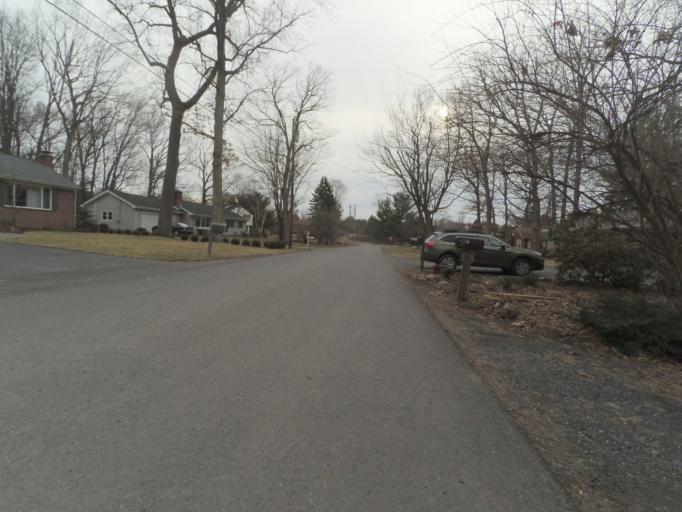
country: US
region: Pennsylvania
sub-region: Centre County
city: State College
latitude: 40.7742
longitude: -77.8516
